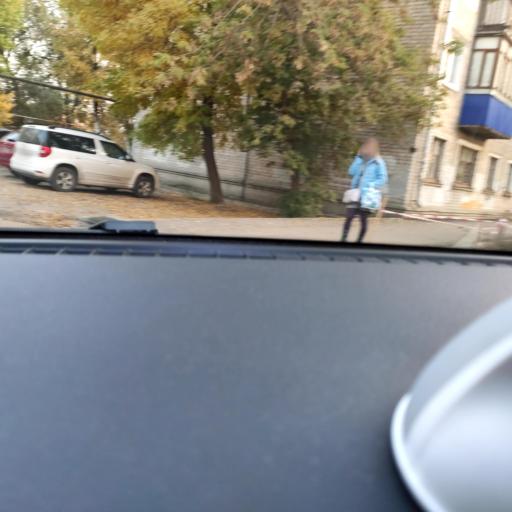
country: RU
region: Samara
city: Petra-Dubrava
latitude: 53.2301
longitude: 50.2843
